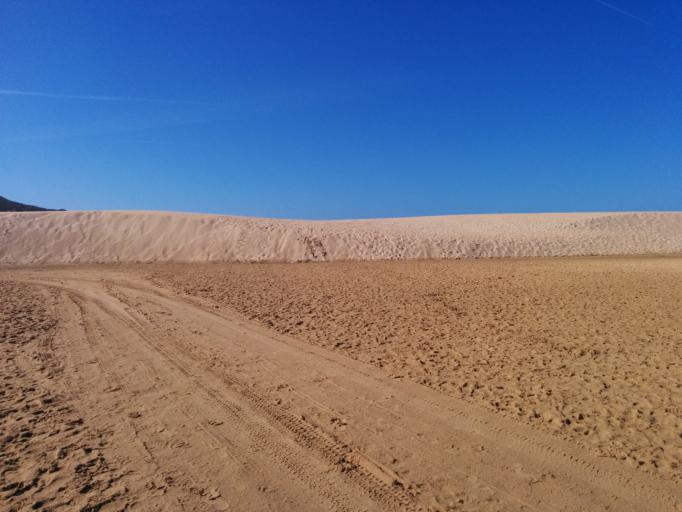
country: PT
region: Faro
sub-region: Vila do Bispo
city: Vila do Bispo
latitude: 37.1948
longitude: -8.9013
